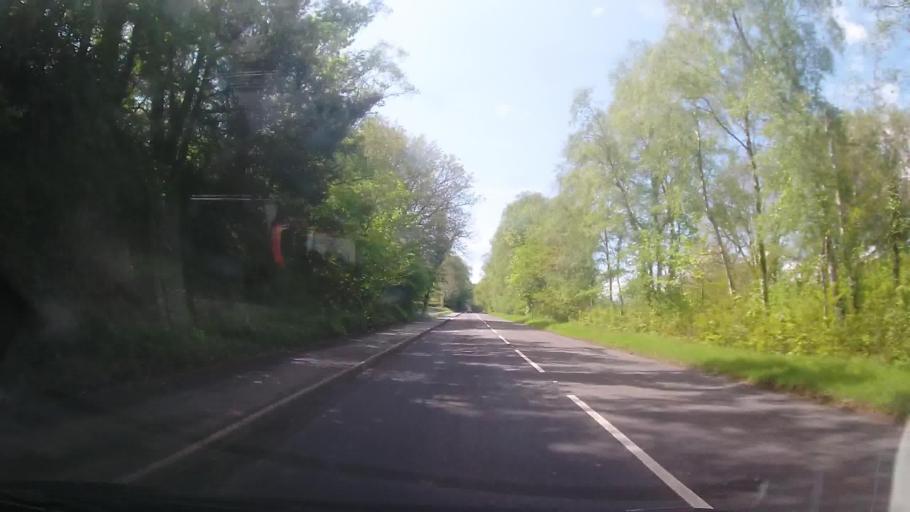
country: GB
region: Wales
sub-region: Gwynedd
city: Porthmadog
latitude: 52.9343
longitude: -4.1575
